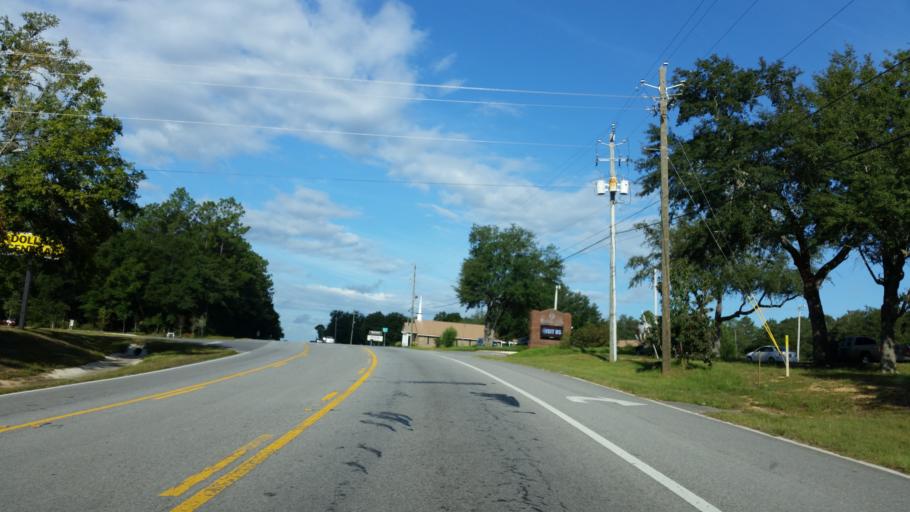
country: US
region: Florida
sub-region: Santa Rosa County
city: Milton
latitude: 30.6467
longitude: -87.0990
